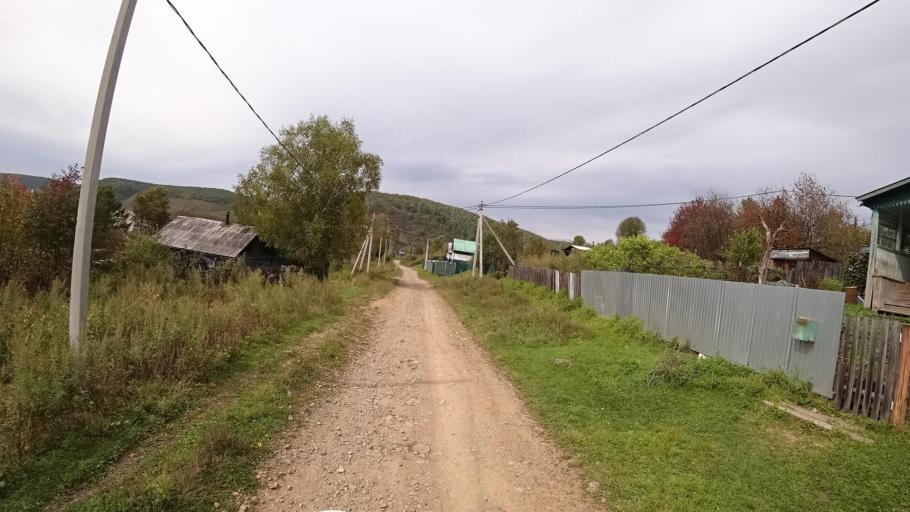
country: RU
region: Jewish Autonomous Oblast
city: Khingansk
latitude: 49.1265
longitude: 131.2031
